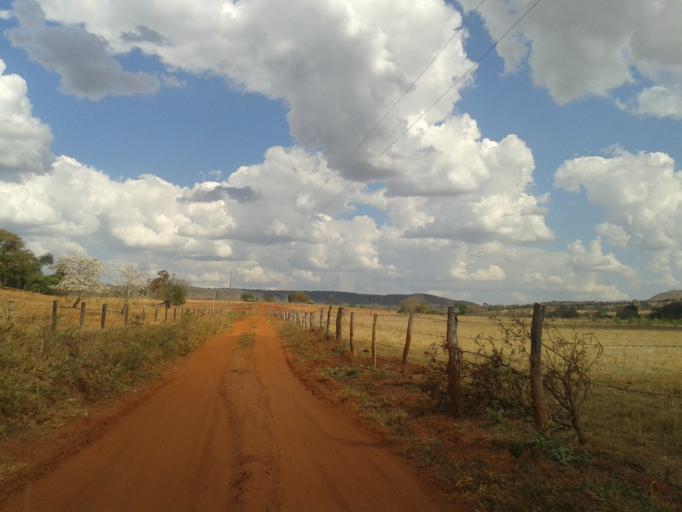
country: BR
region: Minas Gerais
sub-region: Santa Vitoria
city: Santa Vitoria
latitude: -19.1991
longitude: -49.9717
